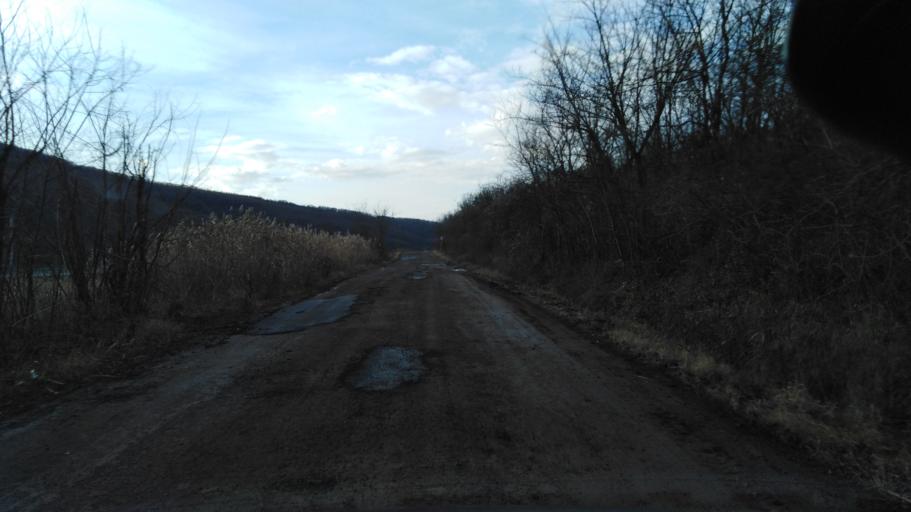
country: HU
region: Nograd
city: Matraverebely
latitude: 47.9705
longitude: 19.7648
